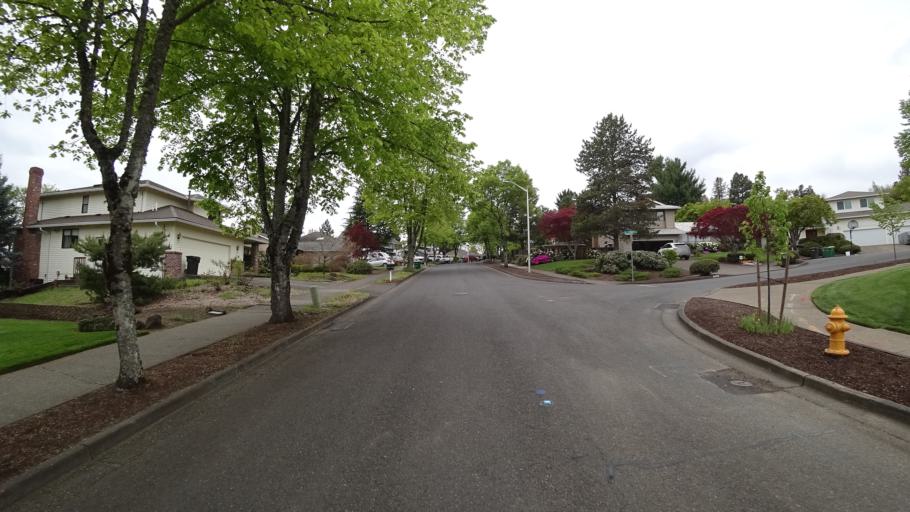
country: US
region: Oregon
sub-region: Washington County
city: Beaverton
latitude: 45.4561
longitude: -122.8217
